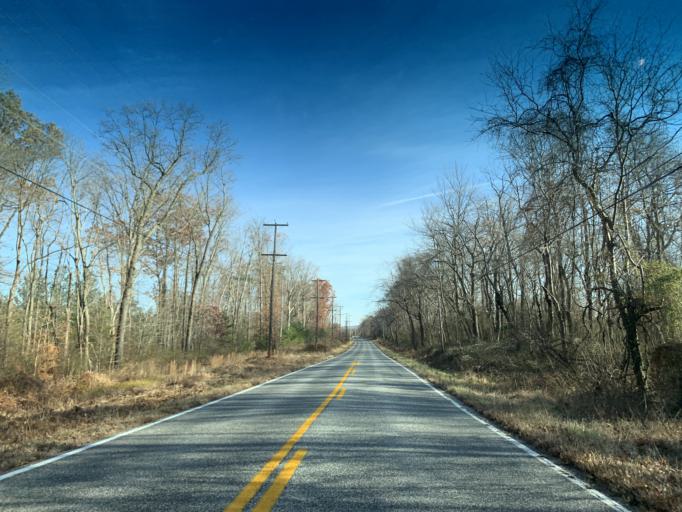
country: US
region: Maryland
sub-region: Cecil County
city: Charlestown
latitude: 39.5814
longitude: -76.0056
